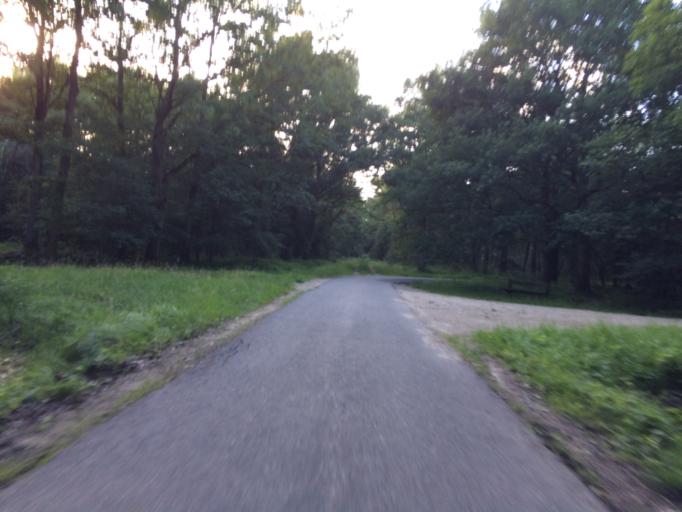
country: FR
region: Ile-de-France
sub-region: Departement de l'Essonne
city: Soisy-sur-Seine
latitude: 48.6724
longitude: 2.4630
